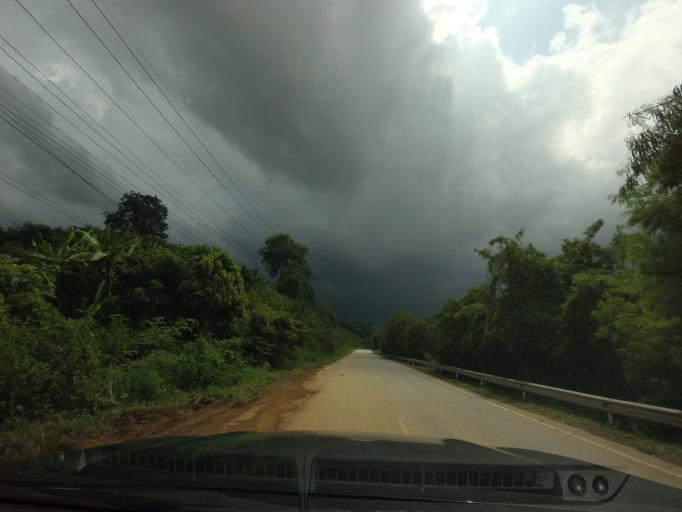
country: LA
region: Vientiane
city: Muang Sanakham
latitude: 17.9746
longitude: 101.7471
